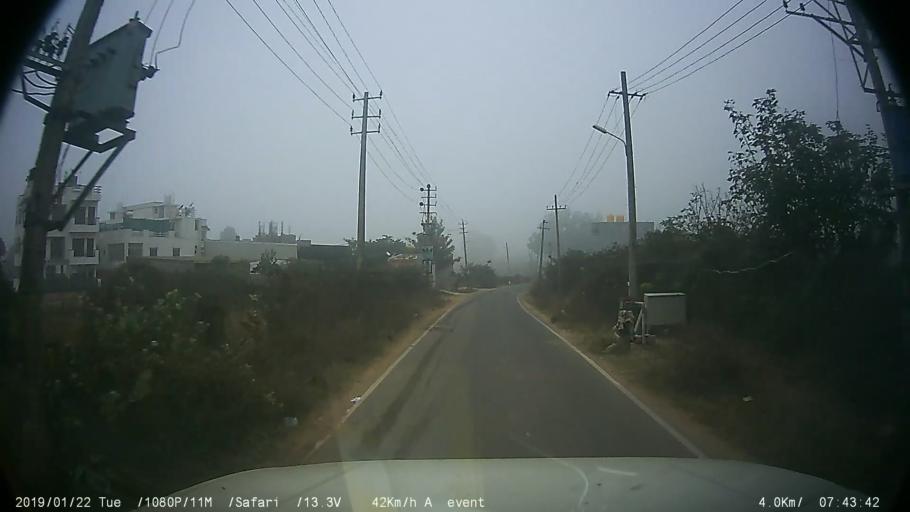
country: IN
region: Karnataka
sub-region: Bangalore Urban
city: Anekal
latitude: 12.8257
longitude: 77.6290
